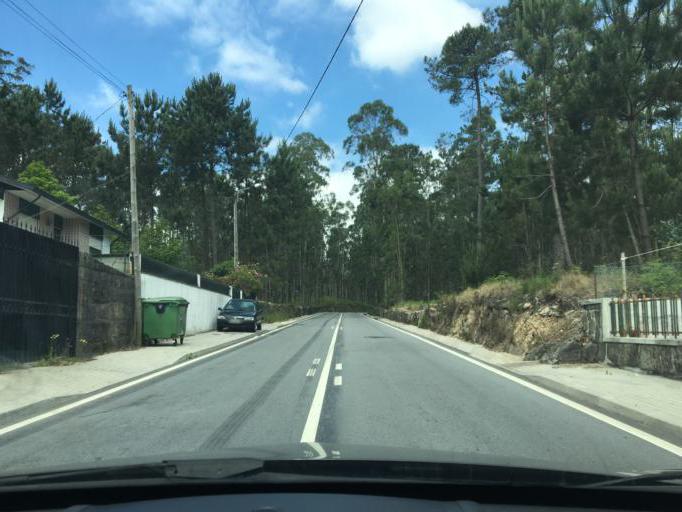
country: PT
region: Porto
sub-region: Maia
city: Anta
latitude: 41.2883
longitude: -8.6061
